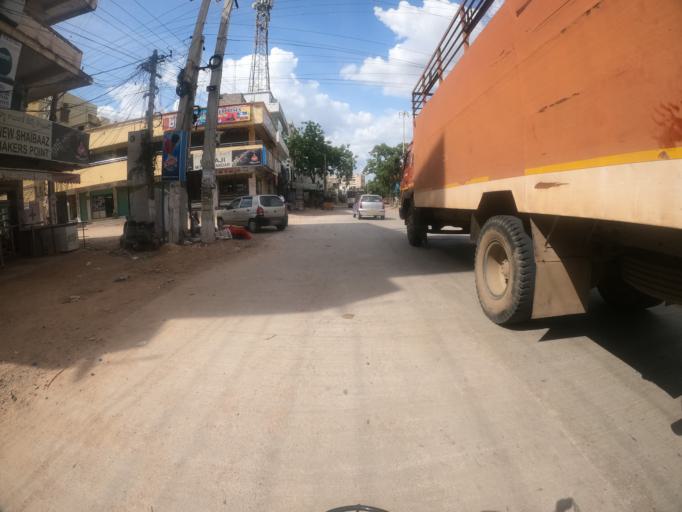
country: IN
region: Telangana
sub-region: Rangareddi
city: Sriramnagar
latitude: 17.3288
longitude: 78.2730
